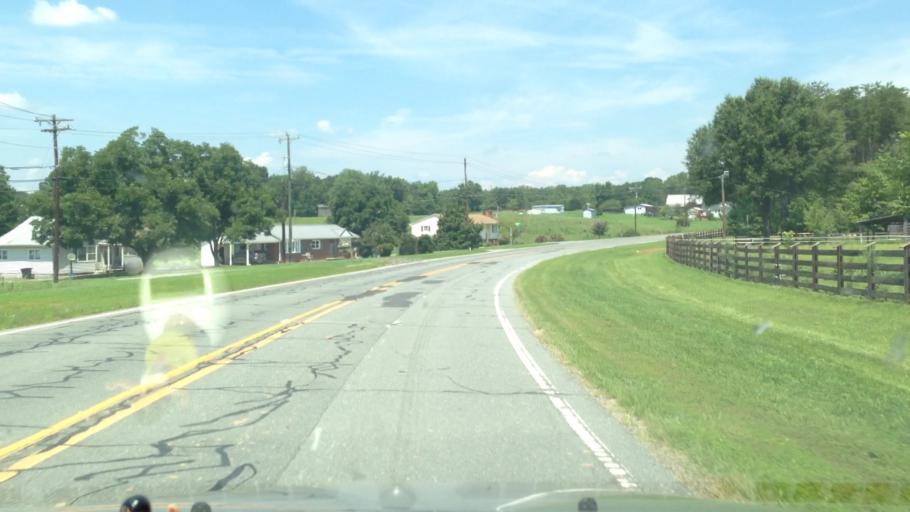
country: US
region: North Carolina
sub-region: Forsyth County
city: Kernersville
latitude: 36.1739
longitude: -80.0603
